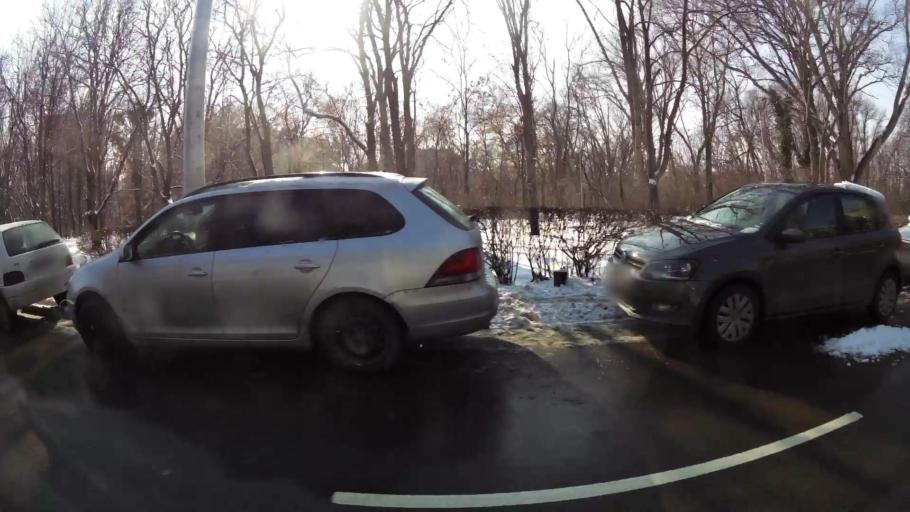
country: BG
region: Sofia-Capital
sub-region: Stolichna Obshtina
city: Sofia
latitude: 42.6744
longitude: 23.3105
